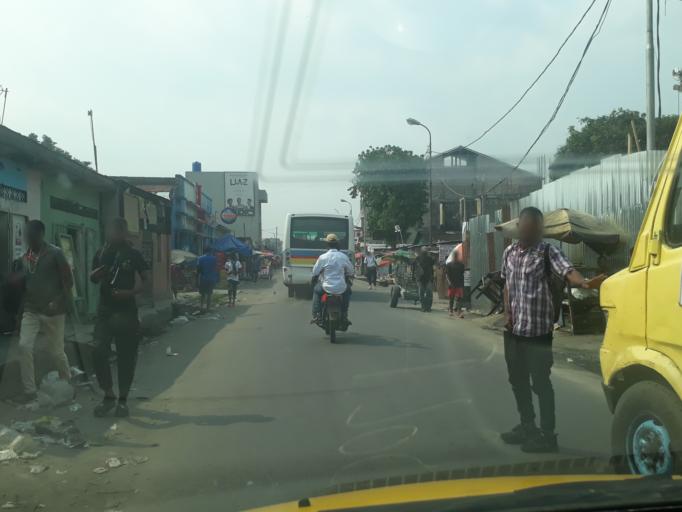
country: CD
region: Kinshasa
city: Kinshasa
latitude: -4.3159
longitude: 15.3194
